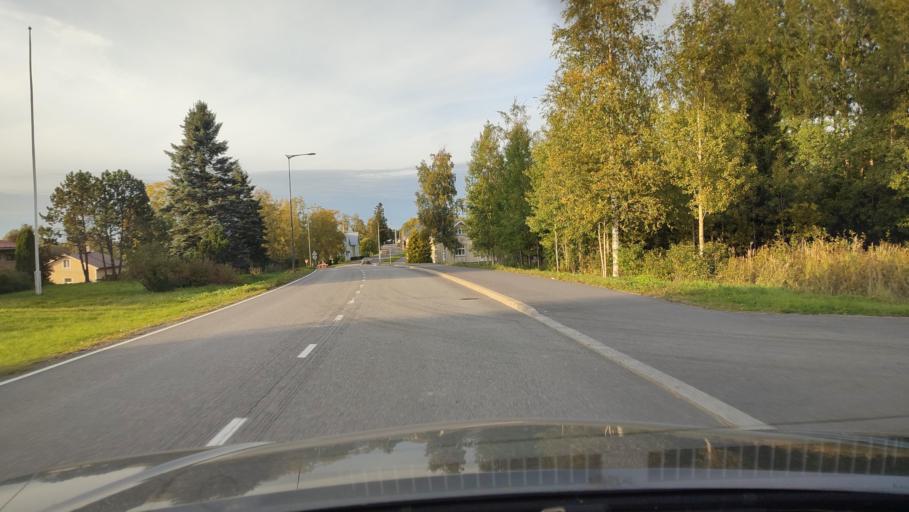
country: FI
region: Ostrobothnia
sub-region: Sydosterbotten
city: Kristinestad
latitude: 62.2477
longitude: 21.5209
